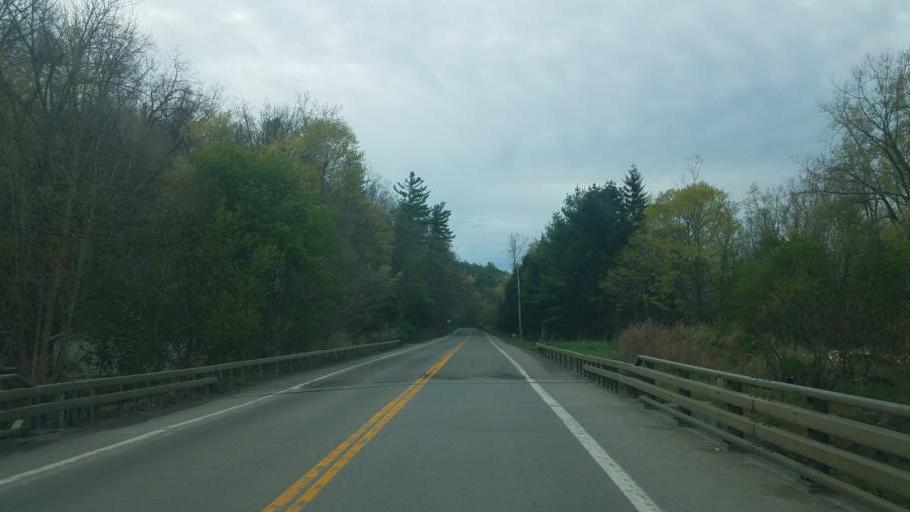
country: US
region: New York
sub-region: Steuben County
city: Canisteo
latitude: 42.2546
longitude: -77.5833
